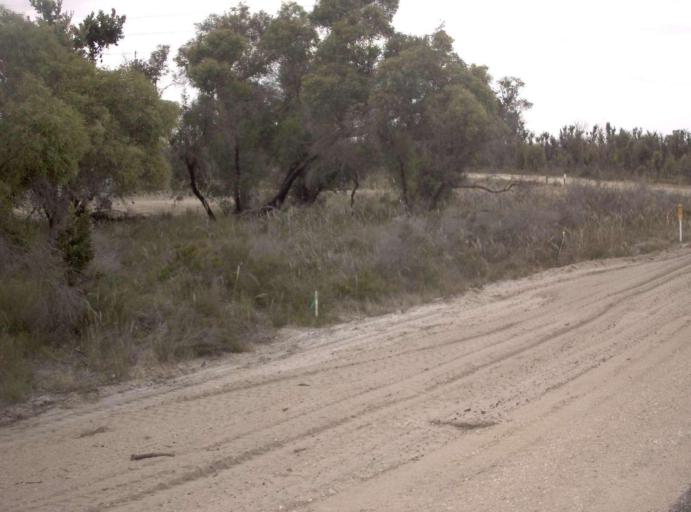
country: AU
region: Victoria
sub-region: East Gippsland
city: Bairnsdale
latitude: -38.1083
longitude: 147.4729
